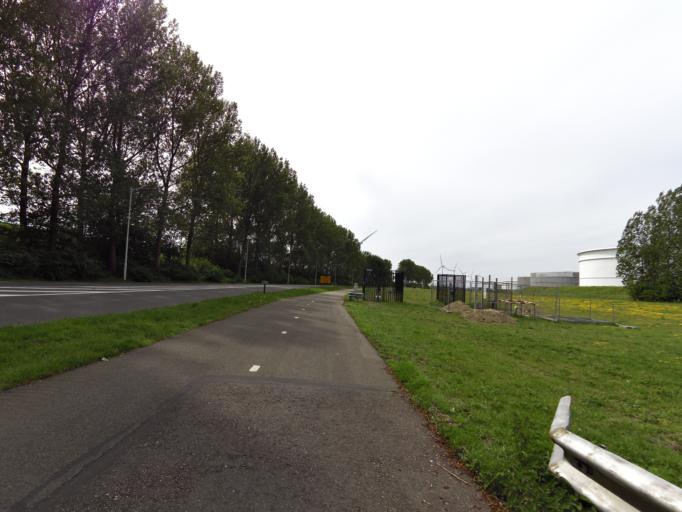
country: NL
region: South Holland
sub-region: Gemeente Maassluis
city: Maassluis
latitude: 51.9015
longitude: 4.2215
